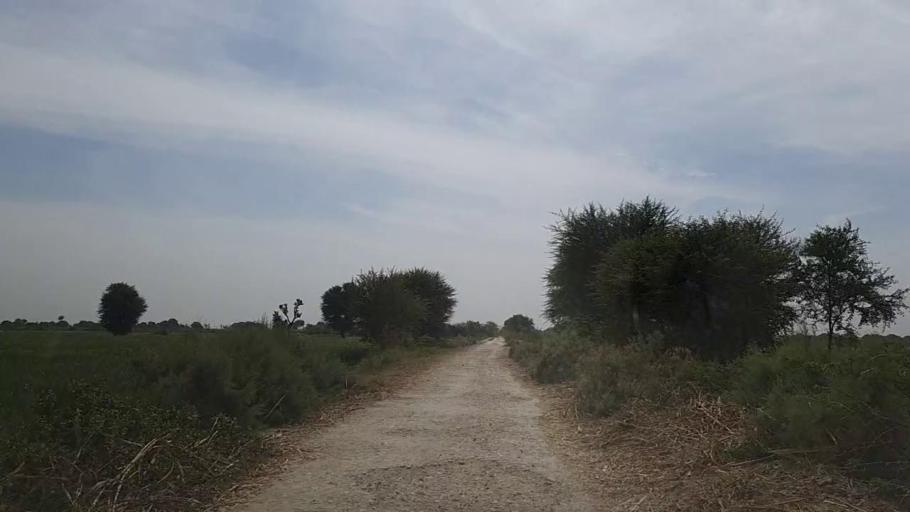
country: PK
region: Sindh
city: Samaro
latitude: 25.2694
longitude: 69.4536
